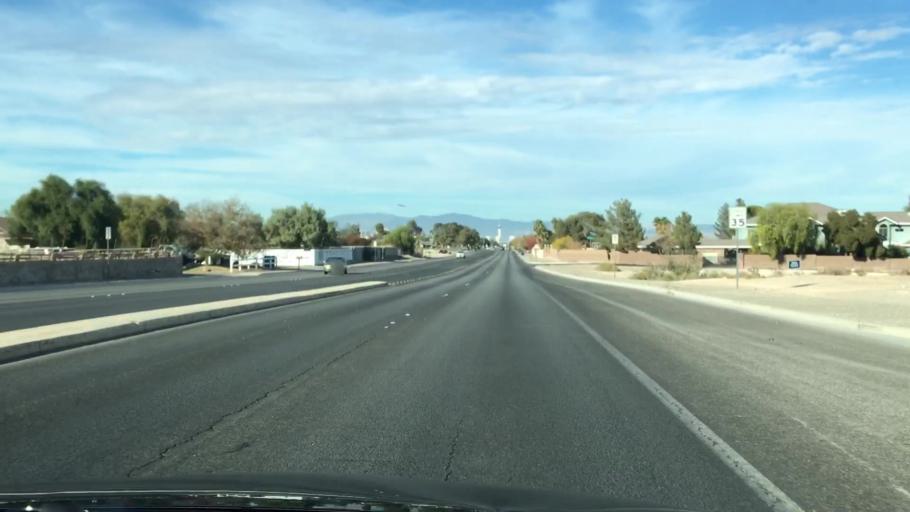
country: US
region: Nevada
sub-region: Clark County
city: Paradise
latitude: 36.0430
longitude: -115.1544
